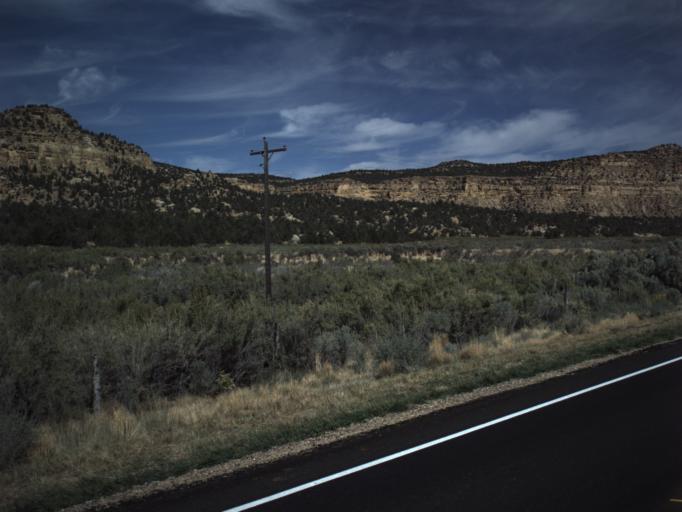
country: US
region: Utah
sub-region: Wayne County
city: Loa
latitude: 37.7487
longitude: -111.7041
